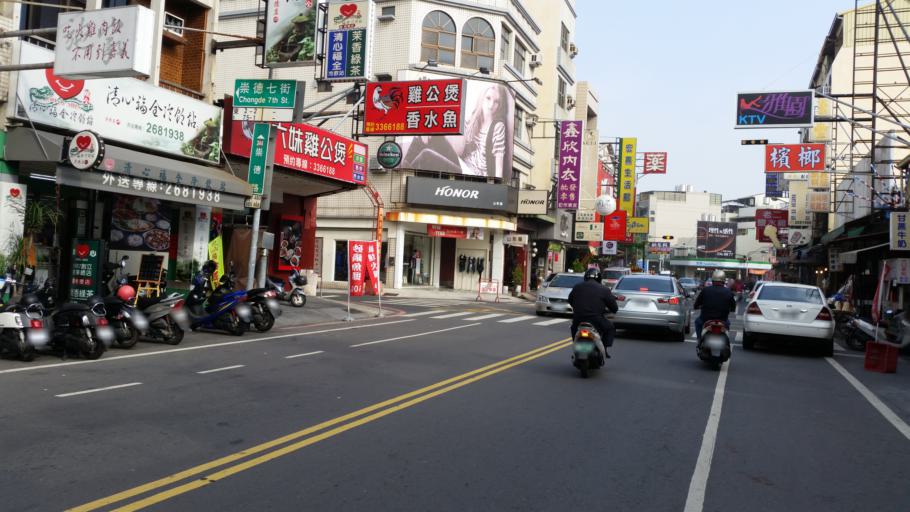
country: TW
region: Taiwan
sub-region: Tainan
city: Tainan
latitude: 22.9746
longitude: 120.2267
